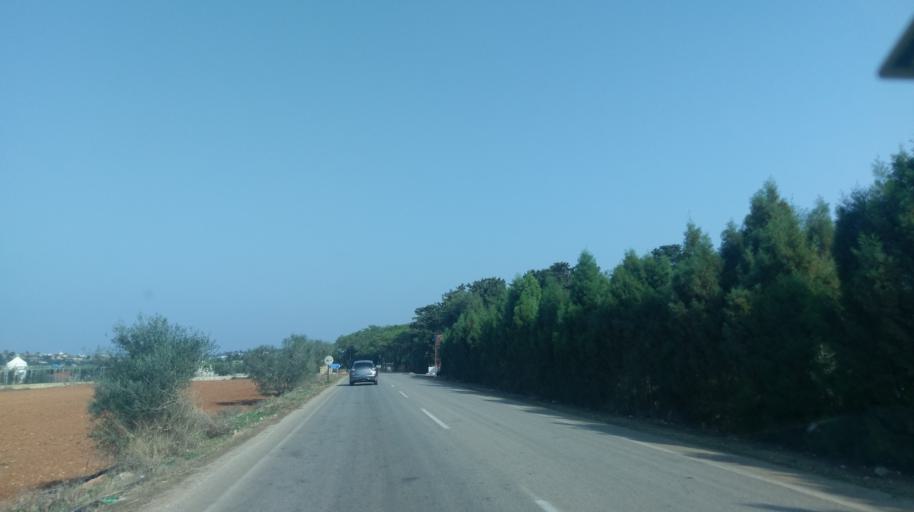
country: CY
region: Ammochostos
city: Leonarisso
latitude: 35.4921
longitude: 34.1556
